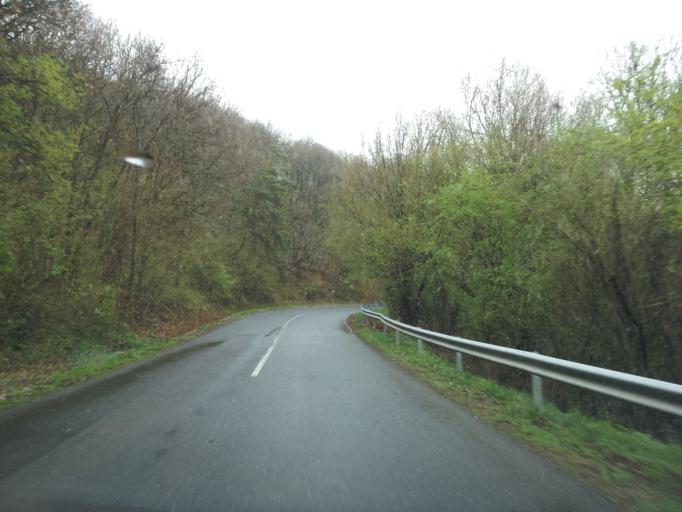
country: HU
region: Borsod-Abauj-Zemplen
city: Rudabanya
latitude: 48.4669
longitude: 20.5232
